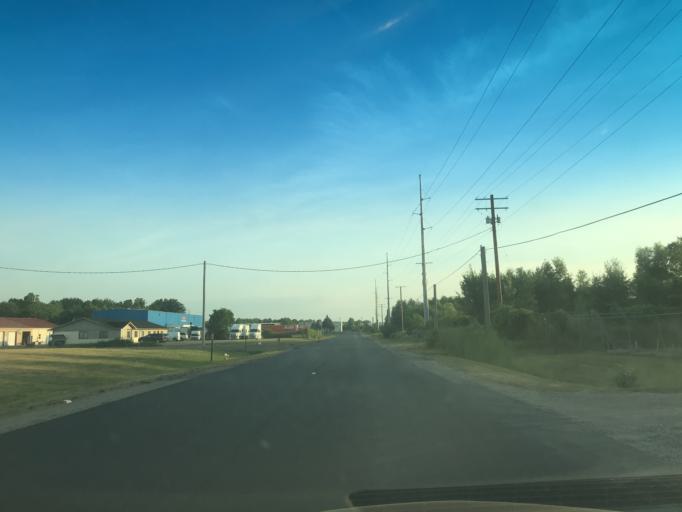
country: US
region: Michigan
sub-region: Eaton County
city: Waverly
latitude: 42.6999
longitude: -84.6312
